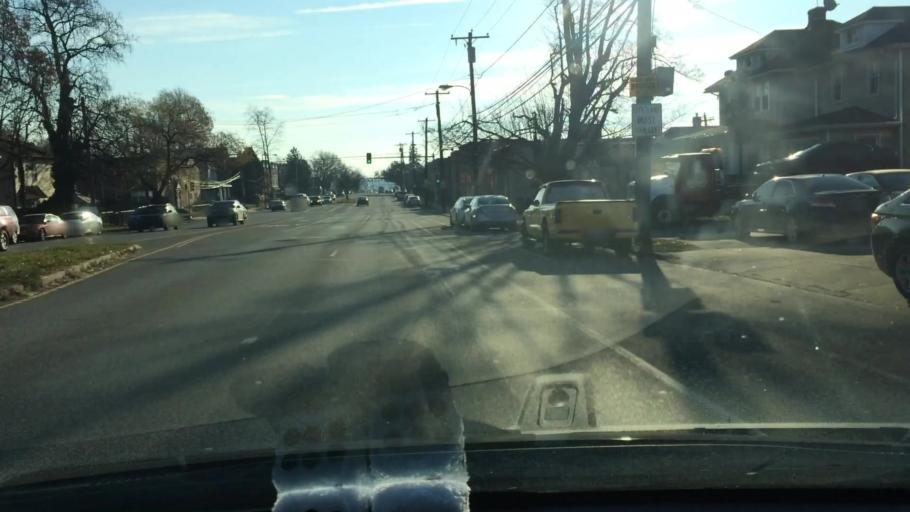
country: US
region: Pennsylvania
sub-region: Montgomery County
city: Rockledge
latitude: 40.0832
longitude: -75.0331
